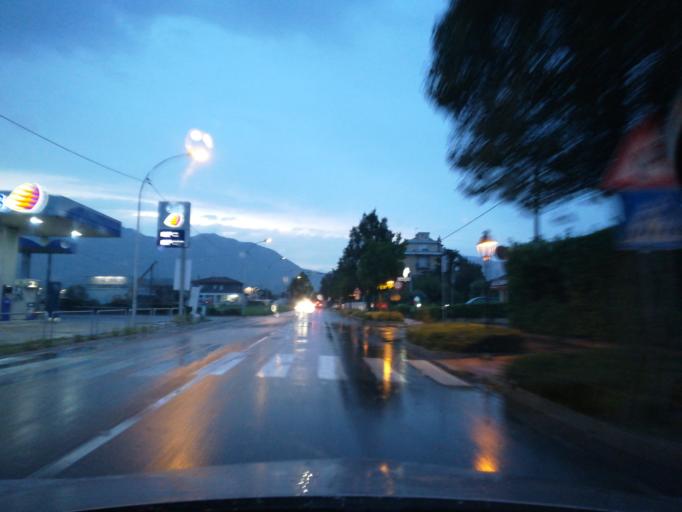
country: IT
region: Lombardy
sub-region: Provincia di Bergamo
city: Brembate di Sopra
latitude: 45.7274
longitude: 9.5836
